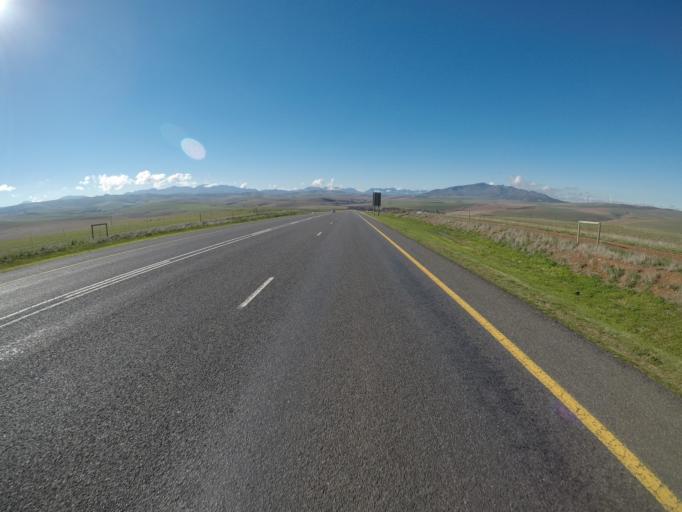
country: ZA
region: Western Cape
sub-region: Overberg District Municipality
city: Caledon
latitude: -34.2171
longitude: 19.3172
